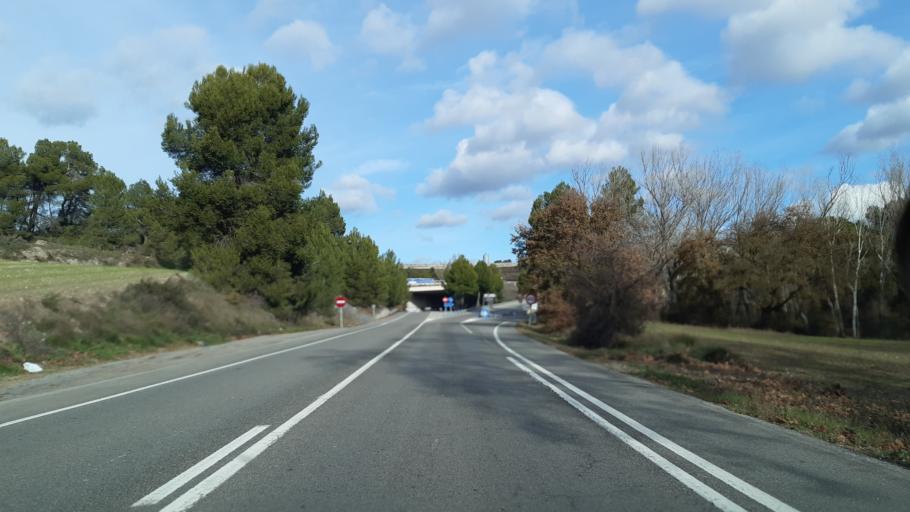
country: ES
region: Catalonia
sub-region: Provincia de Barcelona
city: Odena
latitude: 41.5850
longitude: 1.6724
